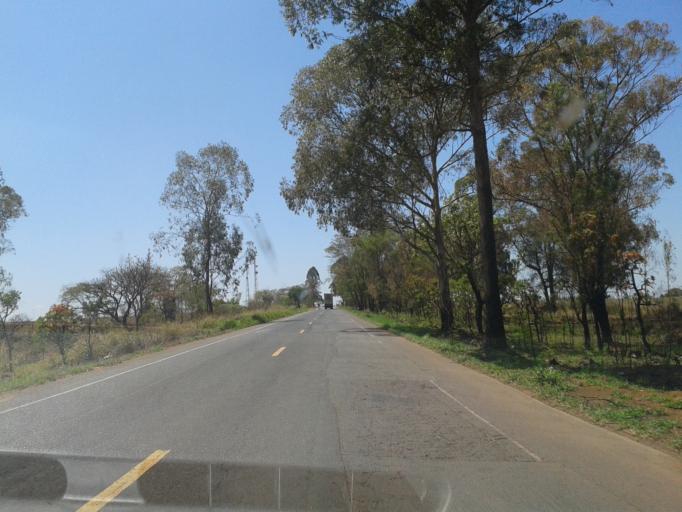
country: BR
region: Minas Gerais
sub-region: Araxa
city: Araxa
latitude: -19.4227
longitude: -47.2590
